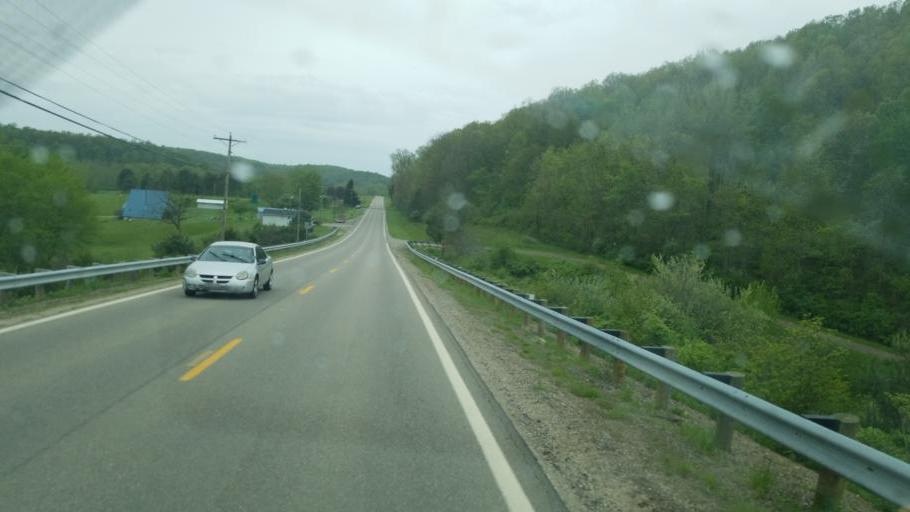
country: US
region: Ohio
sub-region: Guernsey County
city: Cambridge
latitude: 40.1468
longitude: -81.5536
